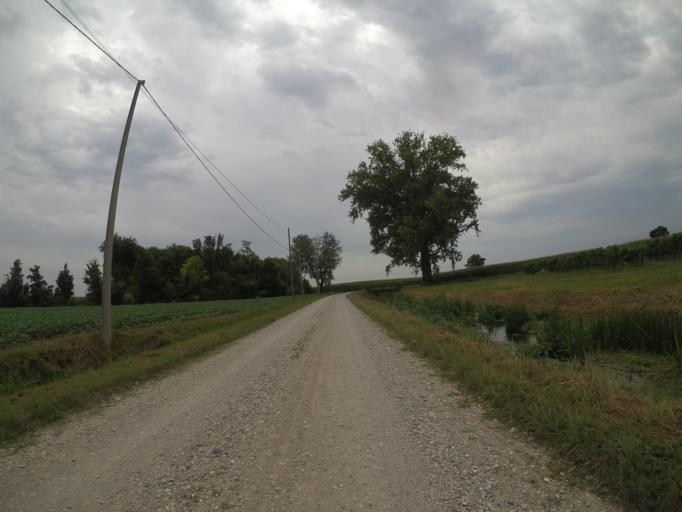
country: IT
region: Friuli Venezia Giulia
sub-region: Provincia di Udine
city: Varmo
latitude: 45.8708
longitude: 13.0015
